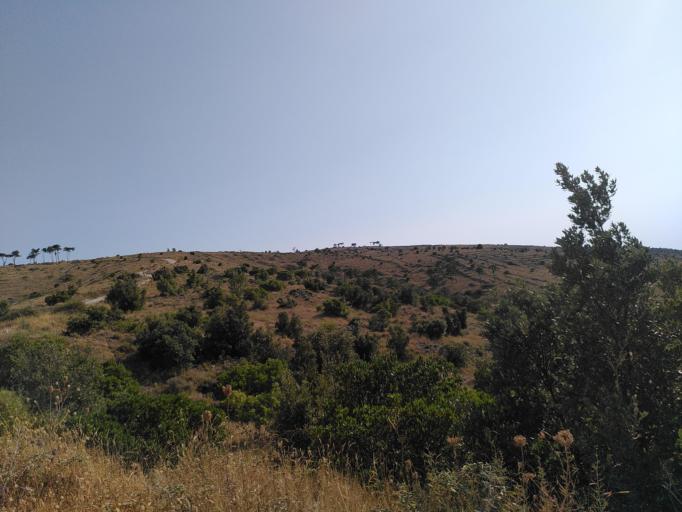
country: HR
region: Splitsko-Dalmatinska
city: Stari Grad
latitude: 43.1525
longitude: 16.5879
